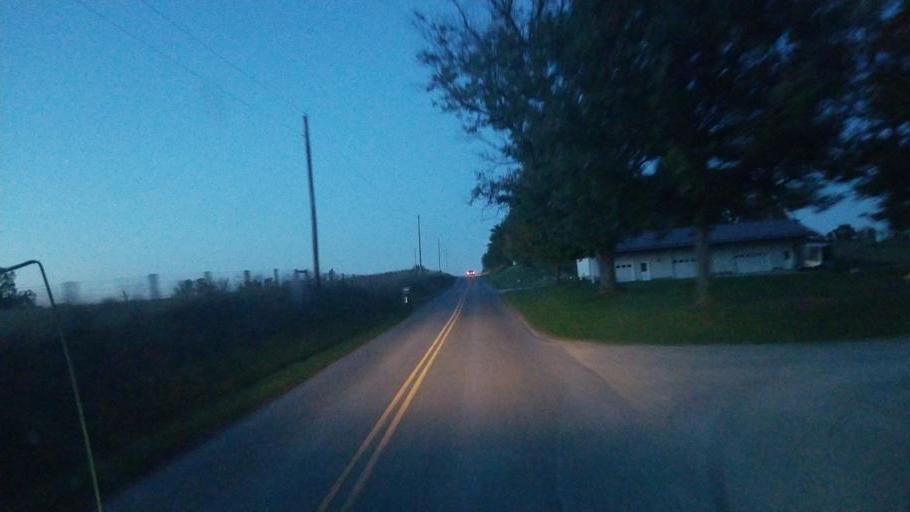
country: US
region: Ohio
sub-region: Perry County
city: Somerset
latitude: 39.8636
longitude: -82.2275
